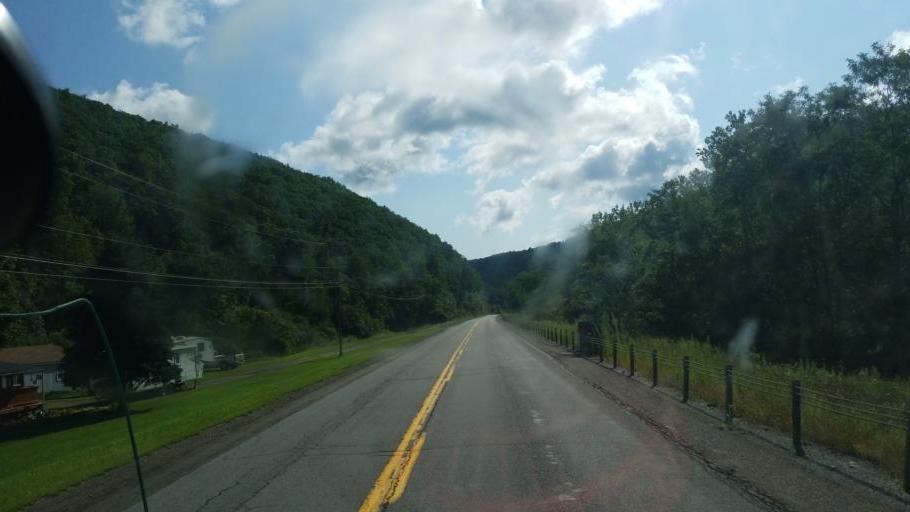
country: US
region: New York
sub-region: Steuben County
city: Canisteo
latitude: 42.2570
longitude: -77.6402
